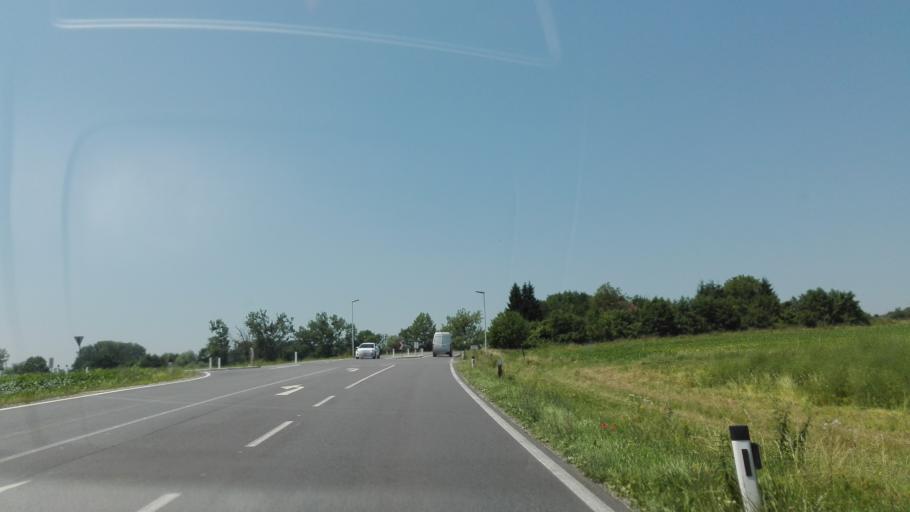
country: AT
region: Upper Austria
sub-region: Politischer Bezirk Linz-Land
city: Pasching
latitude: 48.2691
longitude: 14.2135
